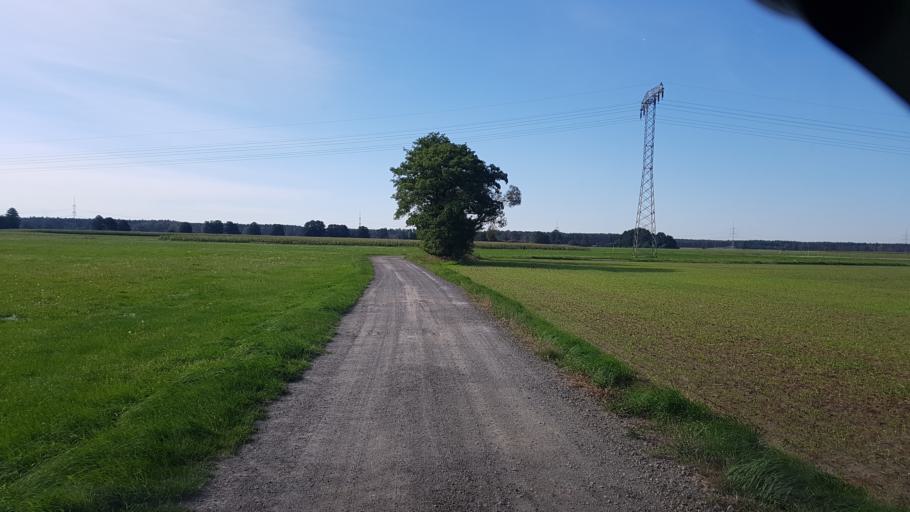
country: DE
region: Brandenburg
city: Sonnewalde
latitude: 51.6707
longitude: 13.6718
